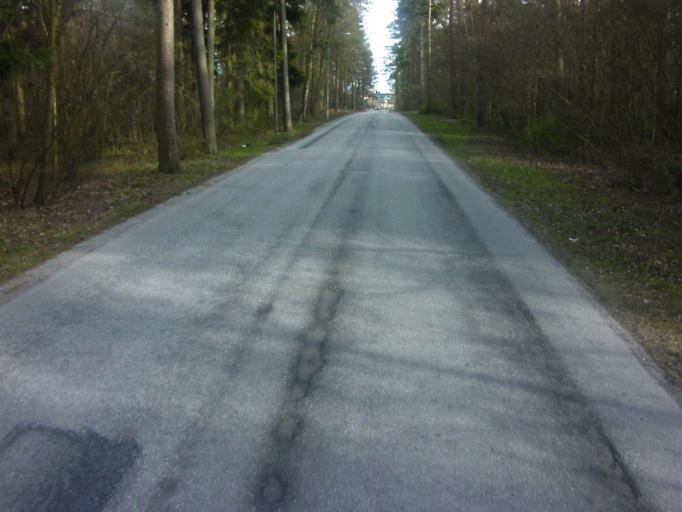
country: SE
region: Skane
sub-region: Kavlinge Kommun
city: Kaevlinge
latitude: 55.7780
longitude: 13.0927
